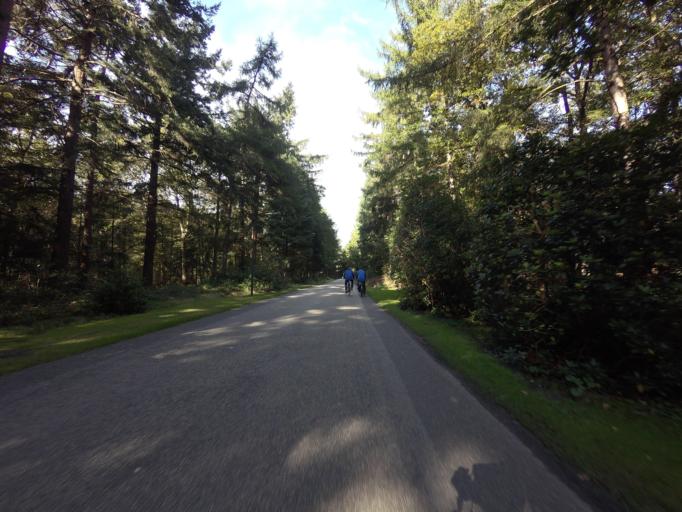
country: NL
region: North Holland
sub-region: Gemeente Wijdemeren
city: Nieuw-Loosdrecht
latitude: 52.2052
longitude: 5.1480
